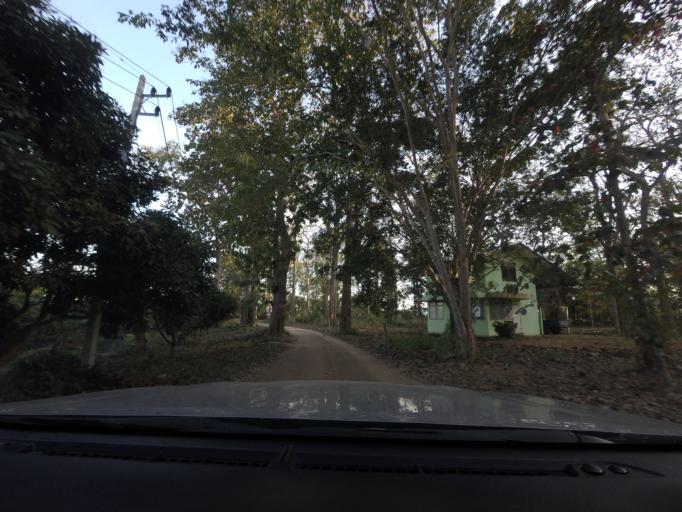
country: TH
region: Chiang Mai
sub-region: Amphoe Chiang Dao
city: Chiang Dao
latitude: 19.3367
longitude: 98.9592
